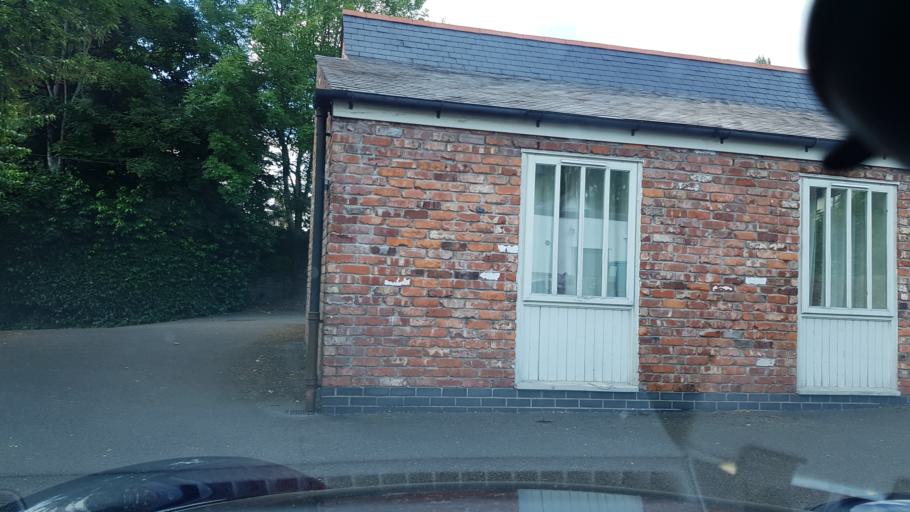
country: GB
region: Wales
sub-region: Monmouthshire
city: Abergavenny
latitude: 51.8131
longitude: -3.0100
